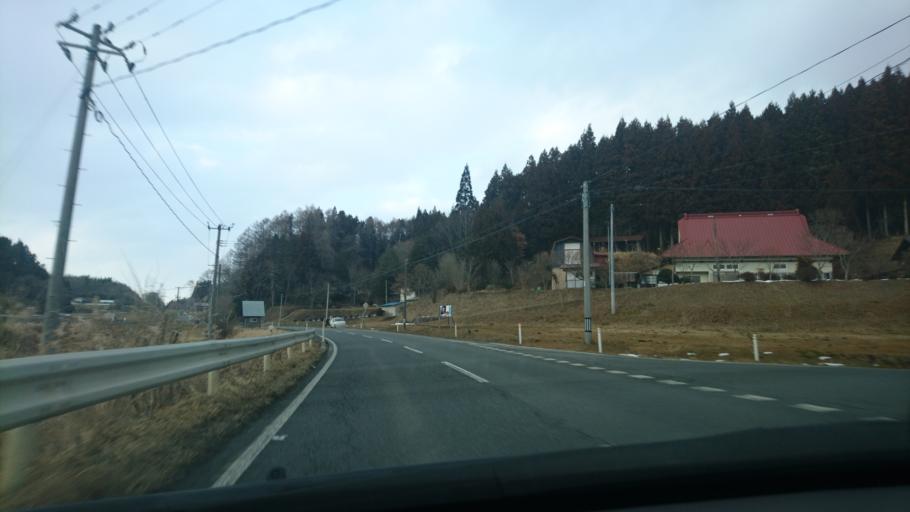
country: JP
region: Iwate
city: Ichinoseki
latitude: 38.9617
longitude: 141.3352
